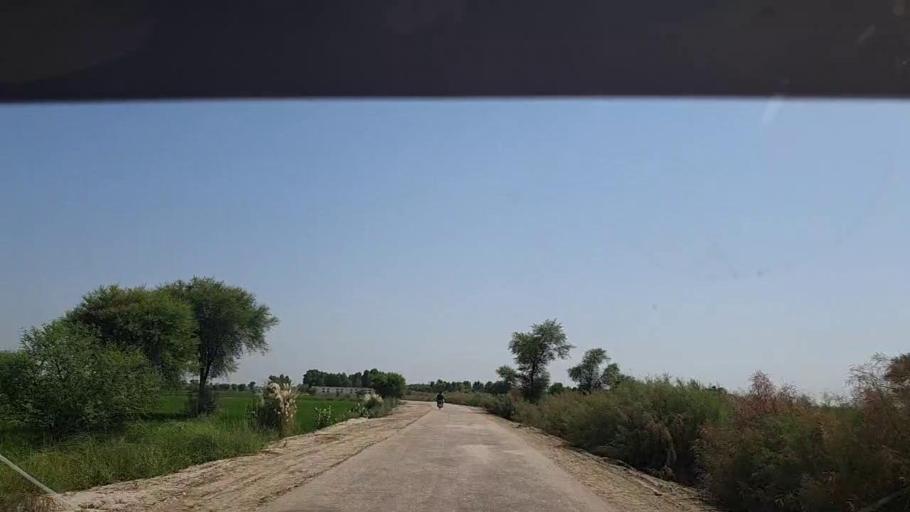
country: PK
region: Sindh
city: Kandhkot
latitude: 28.1672
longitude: 69.1604
